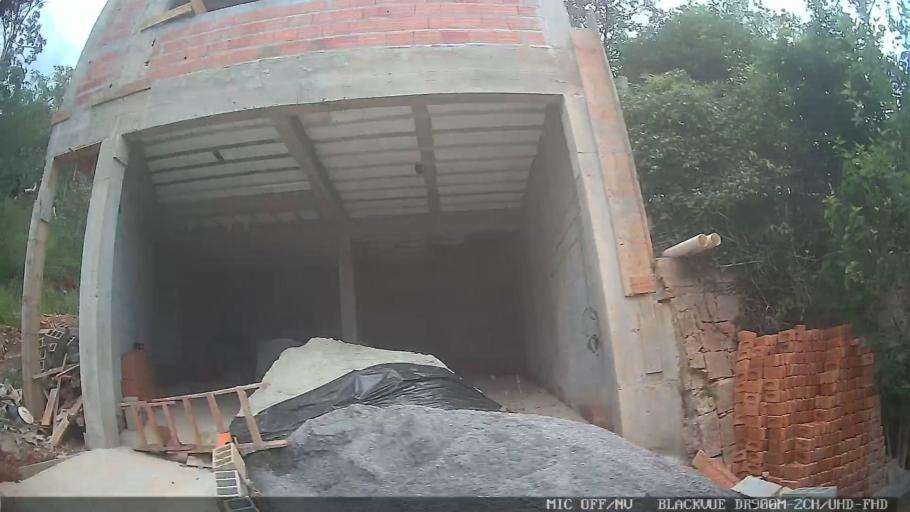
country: BR
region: Minas Gerais
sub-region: Extrema
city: Extrema
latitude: -22.8603
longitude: -46.3162
